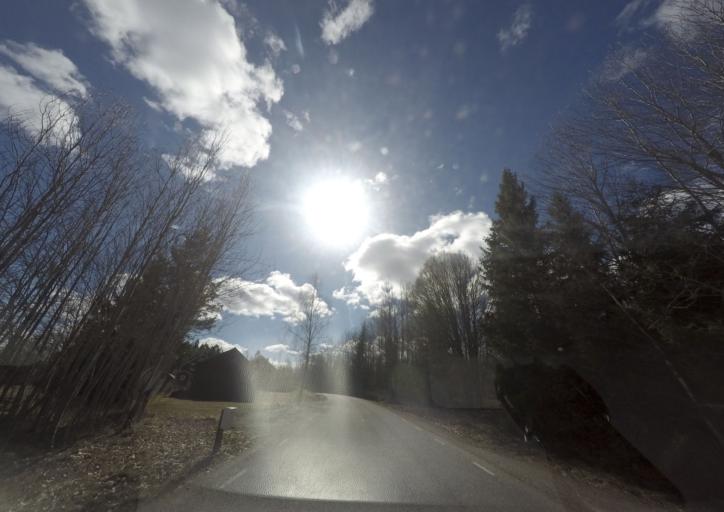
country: SE
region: OEstergoetland
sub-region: Norrkopings Kommun
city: Krokek
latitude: 58.8032
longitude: 16.4553
